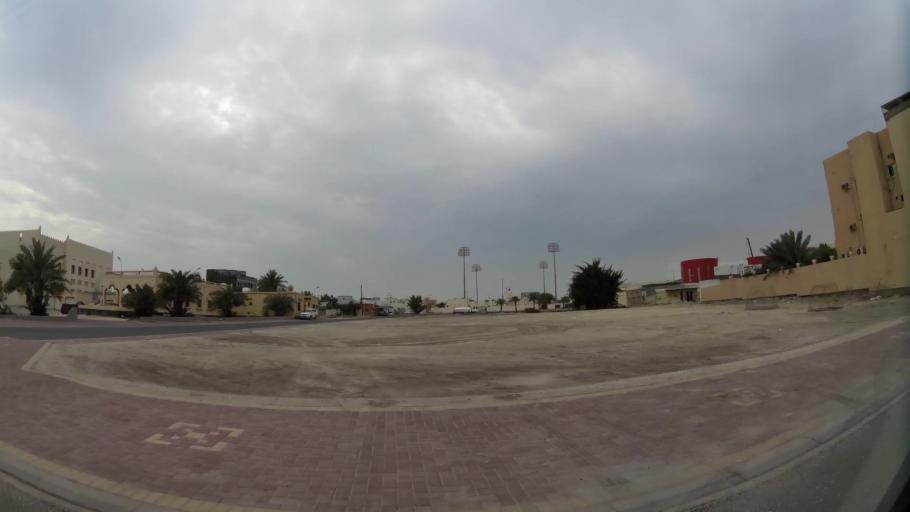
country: BH
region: Northern
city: Ar Rifa'
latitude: 26.0564
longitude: 50.6193
